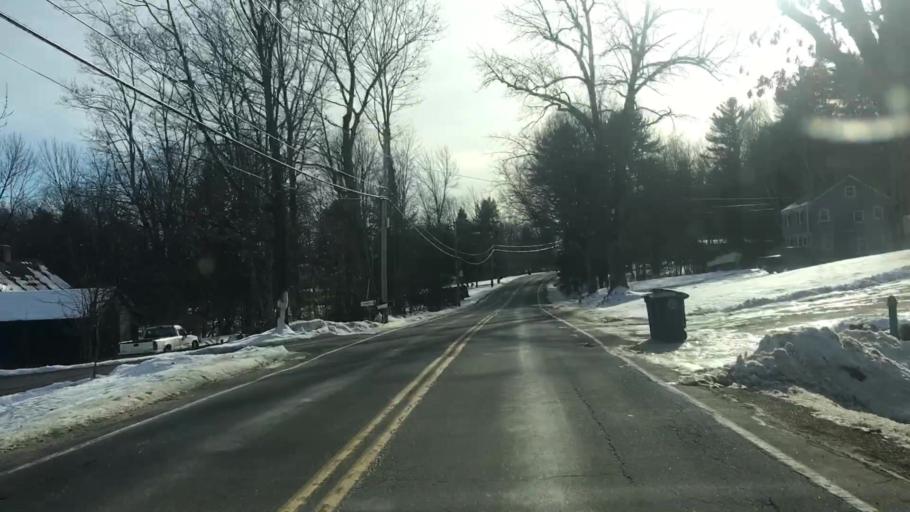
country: US
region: Maine
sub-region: Cumberland County
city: Westbrook
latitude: 43.7214
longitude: -70.3573
